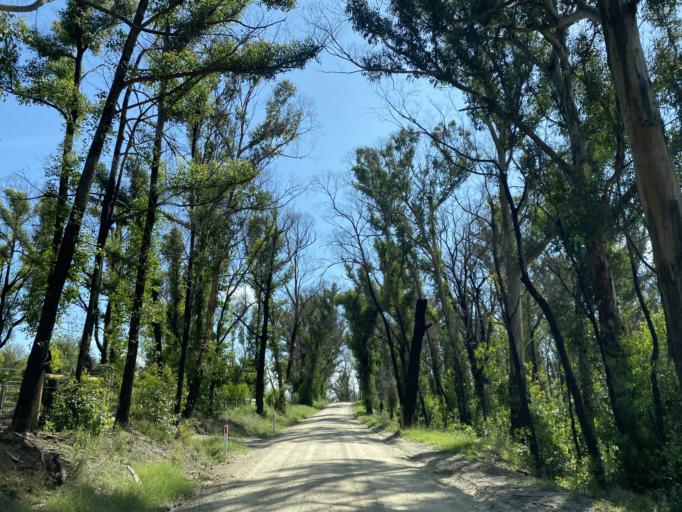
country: AU
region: Victoria
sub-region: Cardinia
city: Garfield
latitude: -38.0427
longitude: 145.6866
